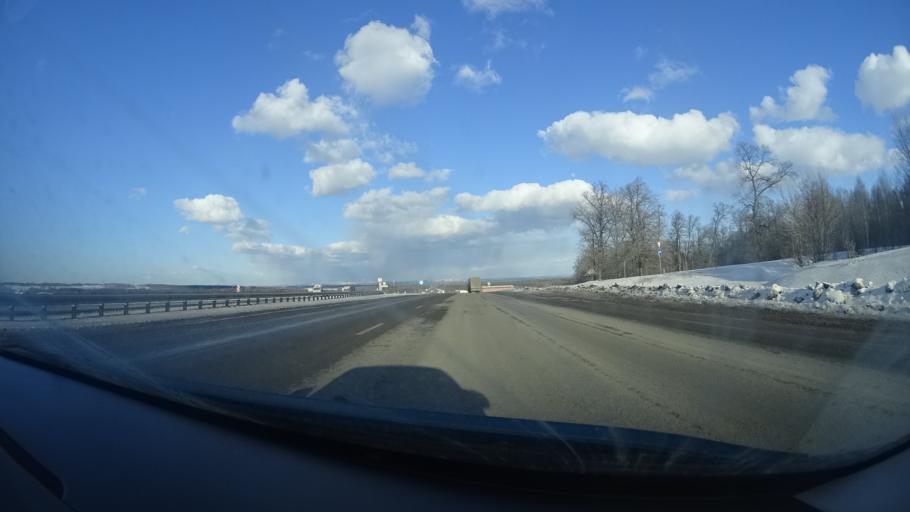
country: RU
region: Bashkortostan
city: Avdon
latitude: 54.6546
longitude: 55.6813
